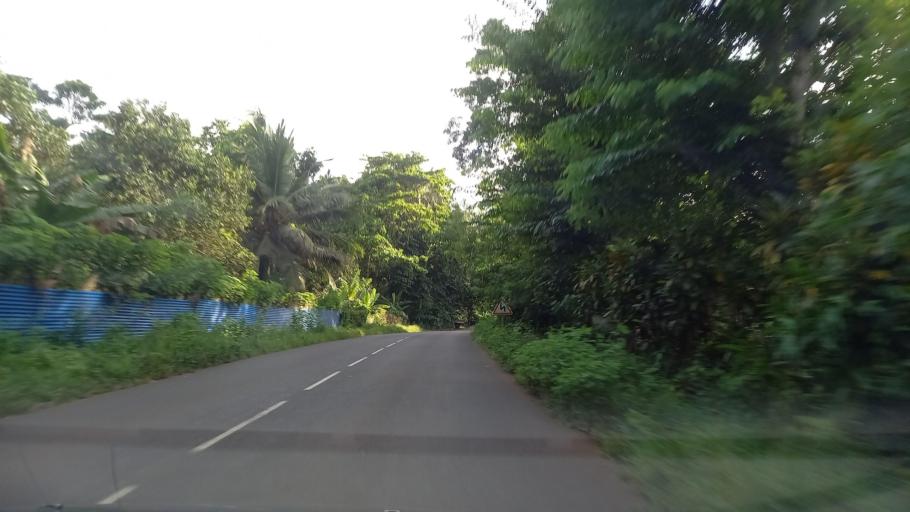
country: YT
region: Bandraboua
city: Bandraboua
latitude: -12.7329
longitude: 45.1193
